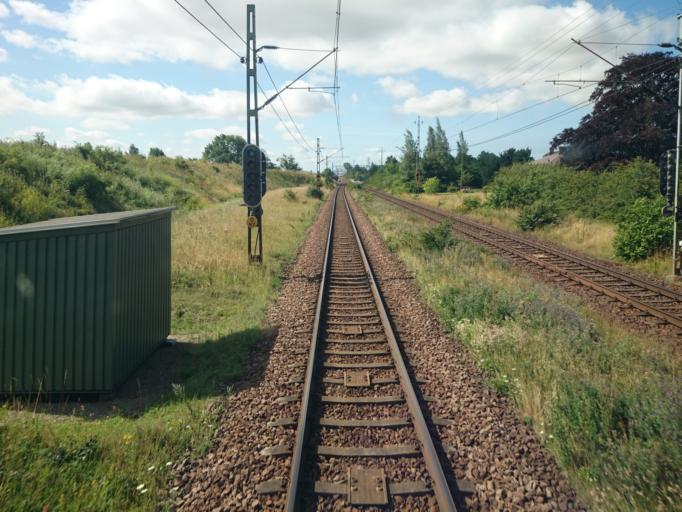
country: SE
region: Skane
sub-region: Lunds Kommun
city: Lund
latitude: 55.7540
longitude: 13.2027
